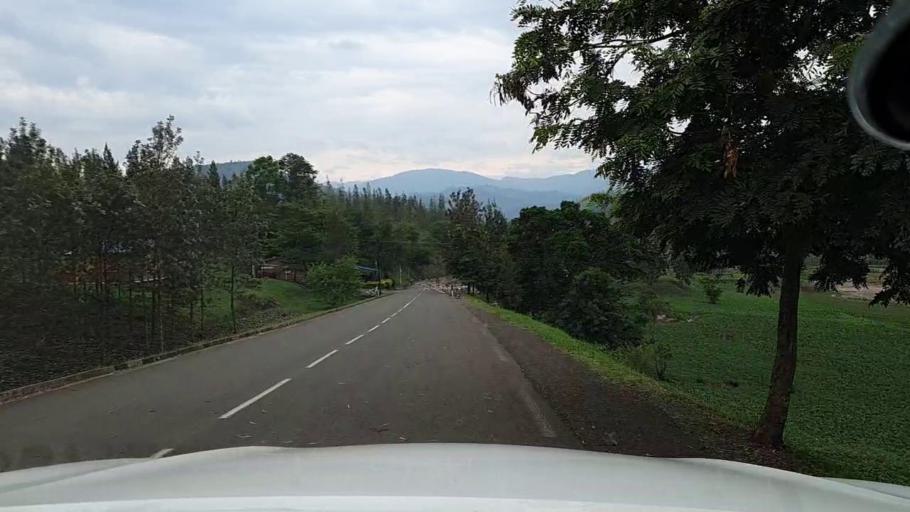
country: BI
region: Cibitoke
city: Cibitoke
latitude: -2.7331
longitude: 29.0390
